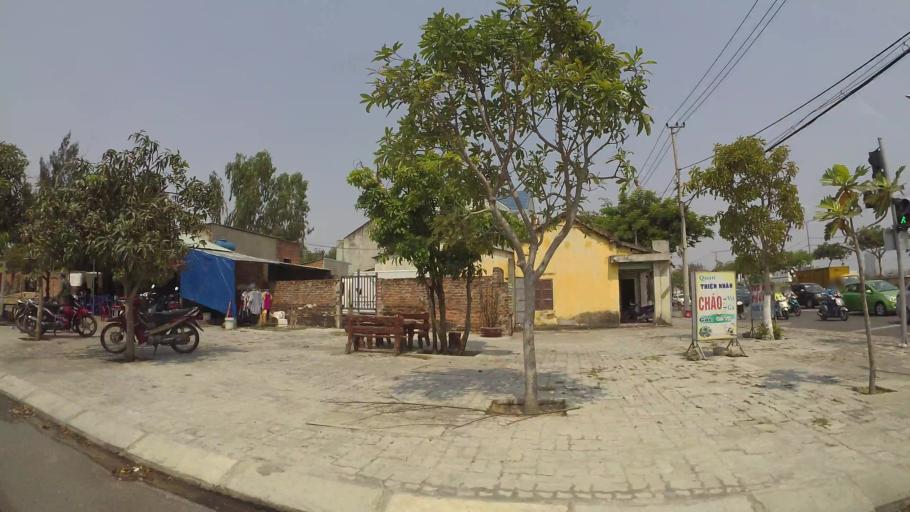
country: VN
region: Da Nang
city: Ngu Hanh Son
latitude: 16.0191
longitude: 108.2524
